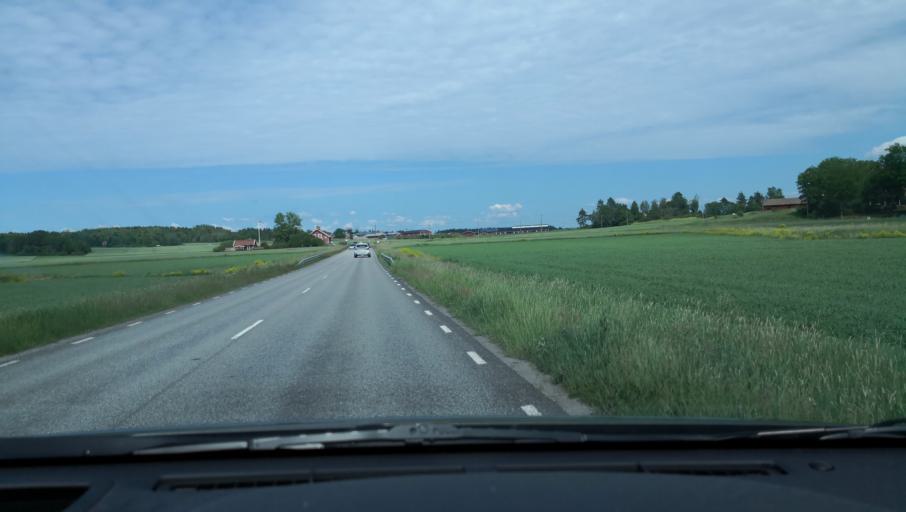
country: SE
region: Stockholm
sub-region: Sigtuna Kommun
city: Sigtuna
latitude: 59.6697
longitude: 17.6947
